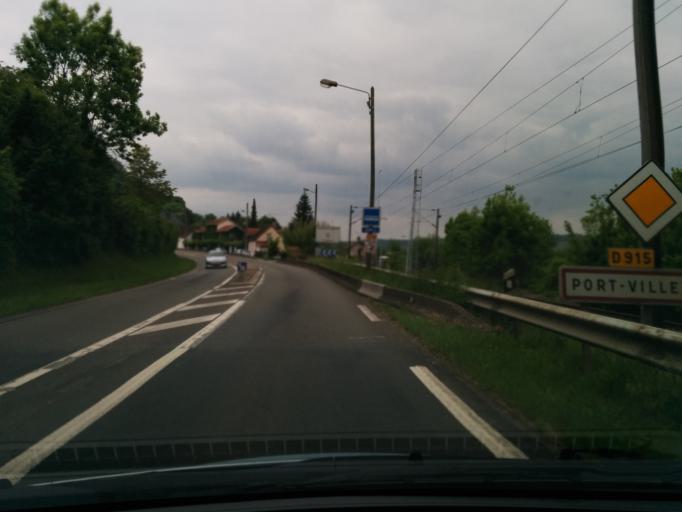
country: FR
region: Ile-de-France
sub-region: Departement des Yvelines
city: Limetz-Villez
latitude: 49.0601
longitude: 1.5249
